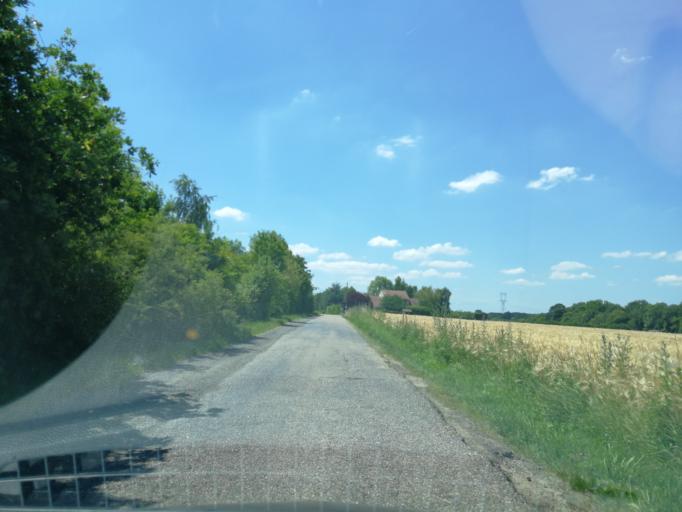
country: FR
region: Ile-de-France
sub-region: Departement de l'Essonne
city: Vaugrigneuse
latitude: 48.6032
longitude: 2.1323
